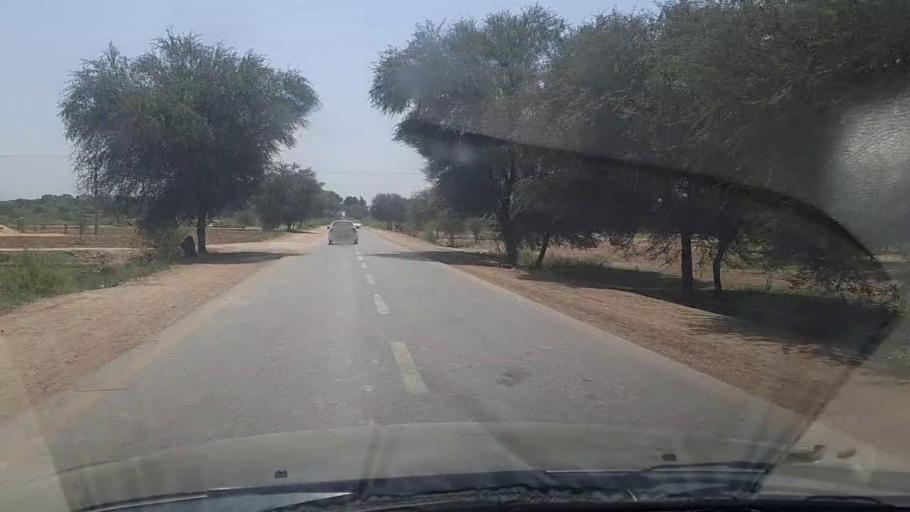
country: PK
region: Sindh
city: Tando Jam
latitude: 25.3058
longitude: 68.5790
